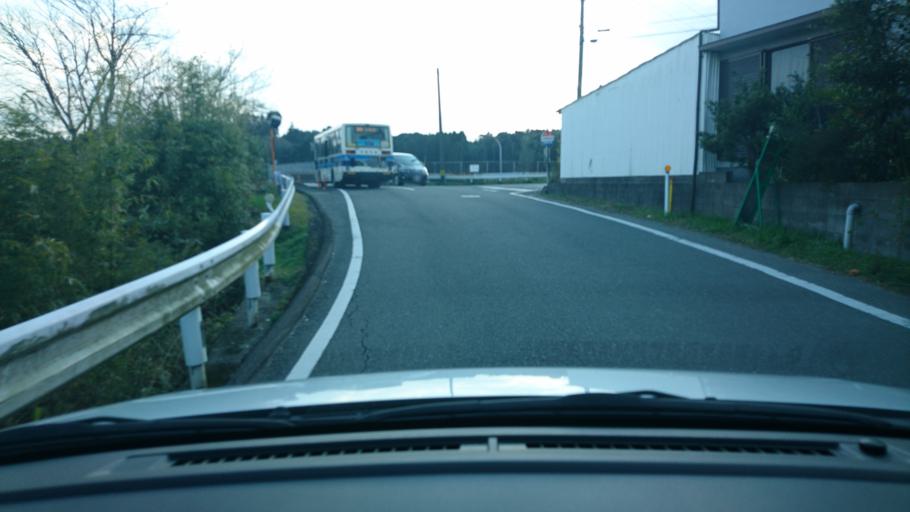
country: JP
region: Miyazaki
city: Miyazaki-shi
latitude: 31.8682
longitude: 131.4038
